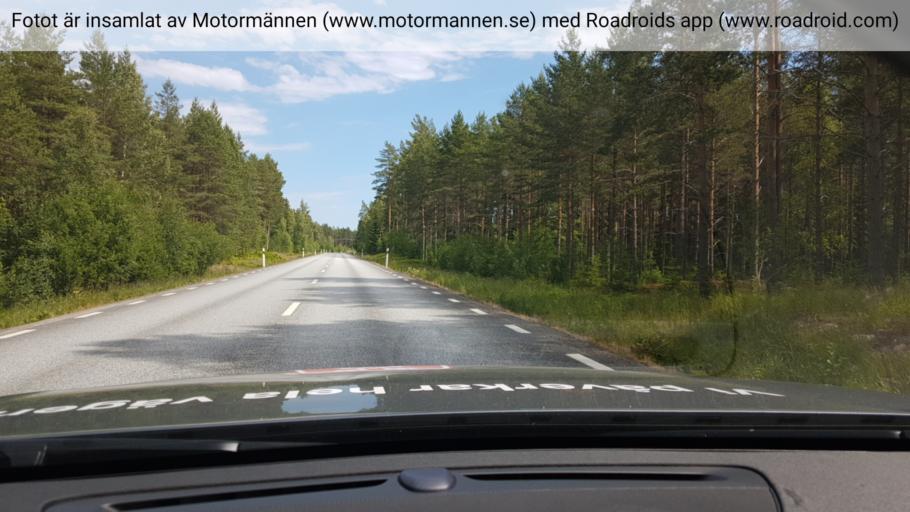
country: SE
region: Uppsala
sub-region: Osthammars Kommun
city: Anneberg
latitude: 60.1744
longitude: 18.4261
